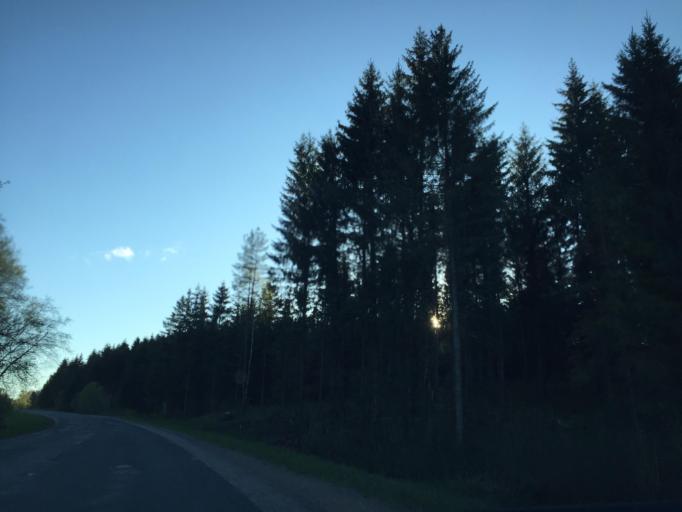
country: LV
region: Ergli
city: Ergli
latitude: 56.8796
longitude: 25.7328
